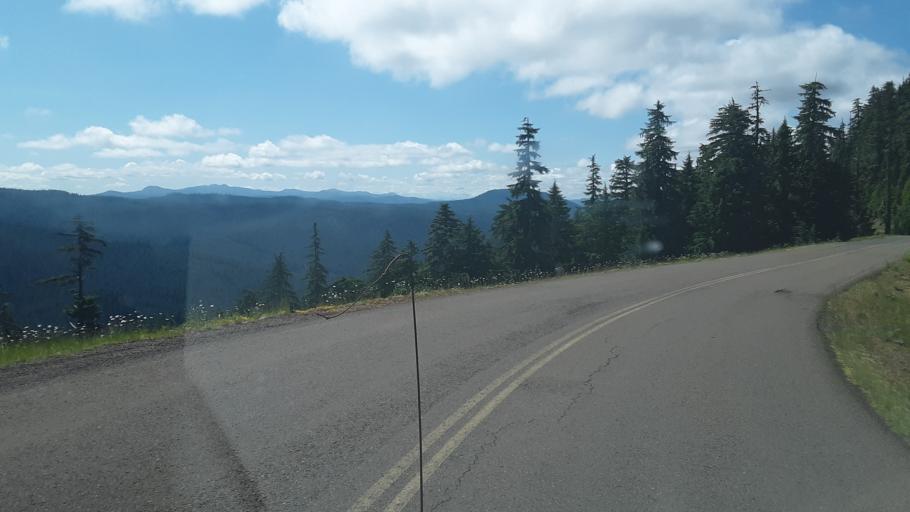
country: US
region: Washington
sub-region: Lewis County
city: Morton
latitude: 46.2690
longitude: -121.9605
